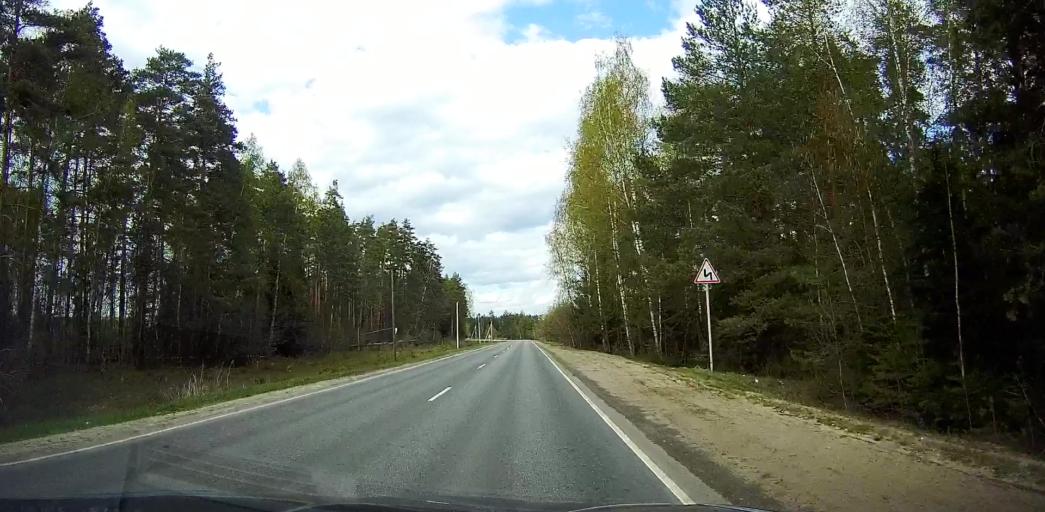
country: RU
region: Moskovskaya
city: Rakhmanovo
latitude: 55.7245
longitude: 38.6274
